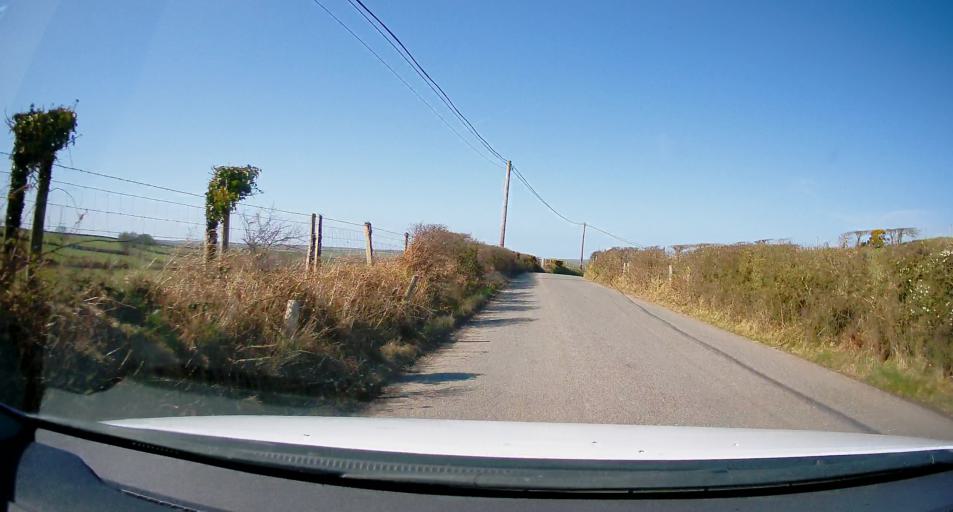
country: GB
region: Wales
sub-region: County of Ceredigion
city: Penparcau
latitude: 52.3249
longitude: -4.0690
